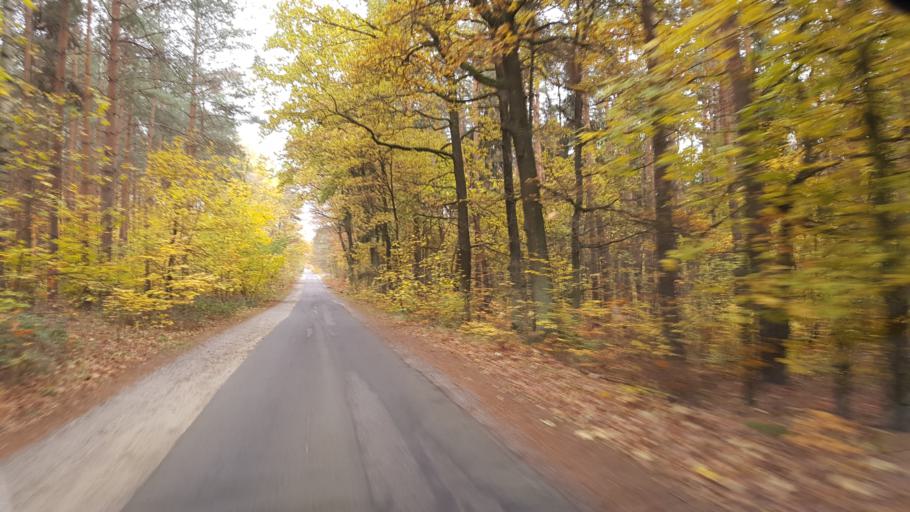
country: DE
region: Brandenburg
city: Crinitz
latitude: 51.7267
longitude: 13.7666
